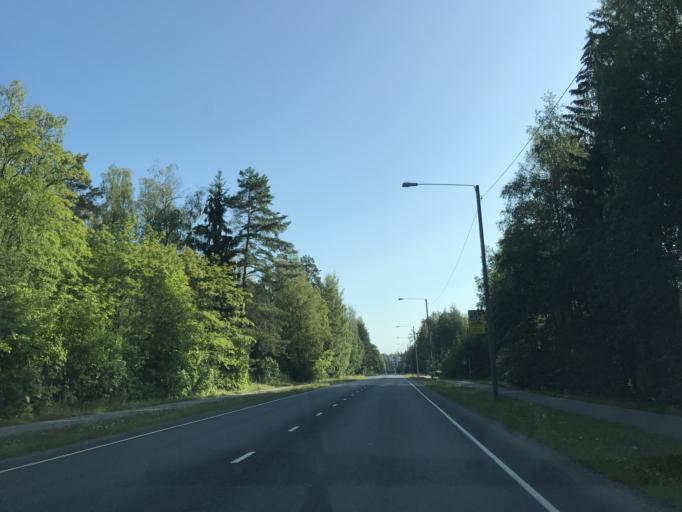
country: FI
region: Paijanne Tavastia
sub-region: Lahti
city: Orimattila
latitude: 60.7974
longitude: 25.7239
